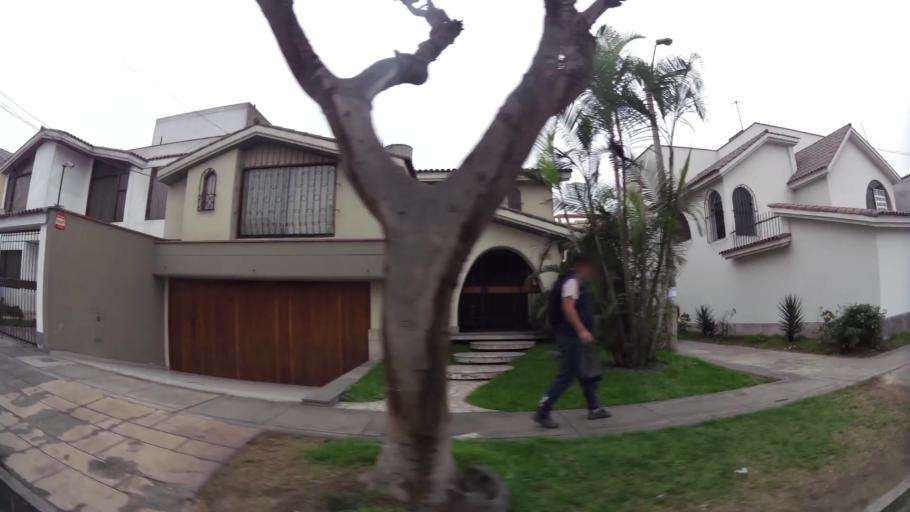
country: PE
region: Lima
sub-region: Lima
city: La Molina
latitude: -12.0704
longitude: -76.9603
